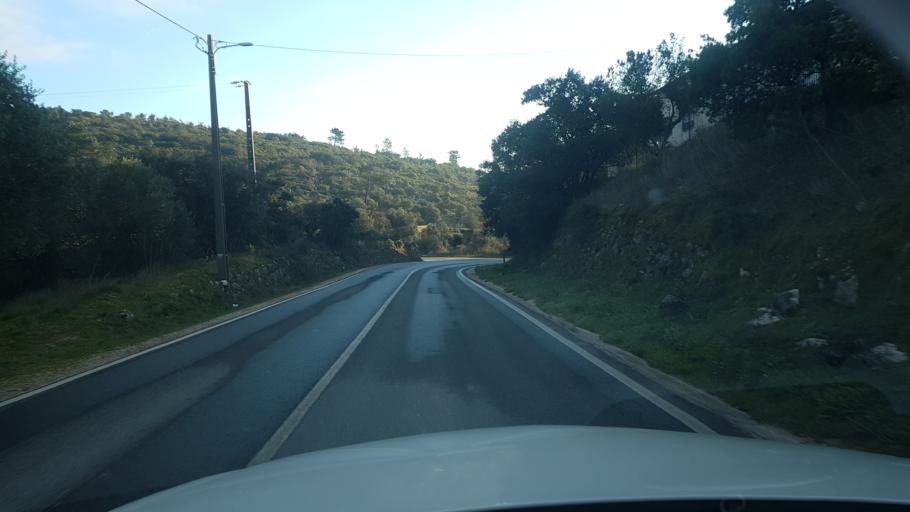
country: PT
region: Santarem
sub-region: Ourem
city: Ourem
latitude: 39.5729
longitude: -8.5892
